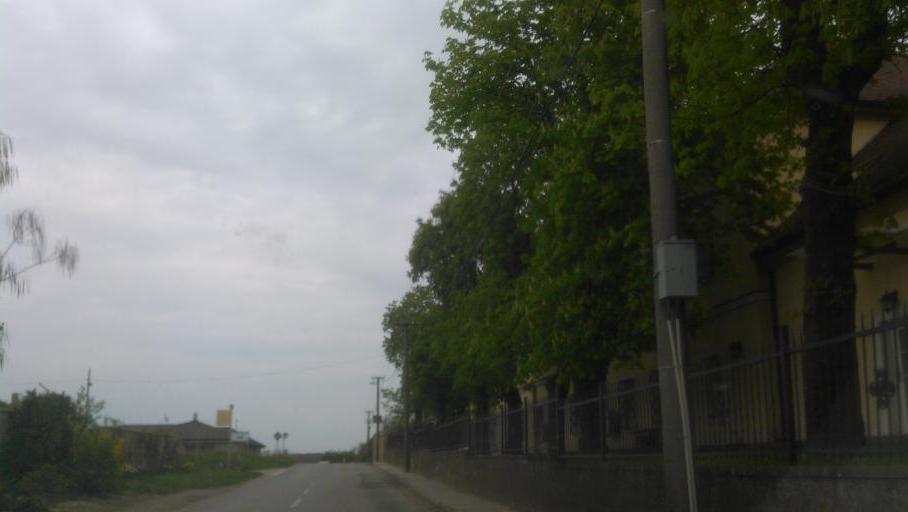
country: SK
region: Bratislavsky
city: Dunajska Luzna
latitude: 48.1301
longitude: 17.2964
